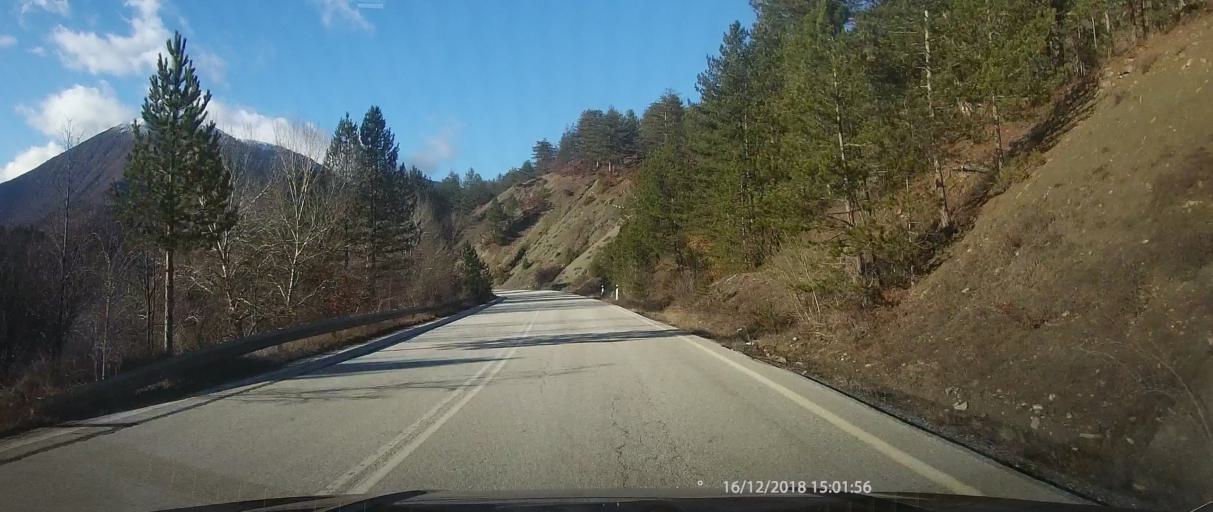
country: GR
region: West Macedonia
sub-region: Nomos Kastorias
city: Nestorio
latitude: 40.2260
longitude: 21.0013
